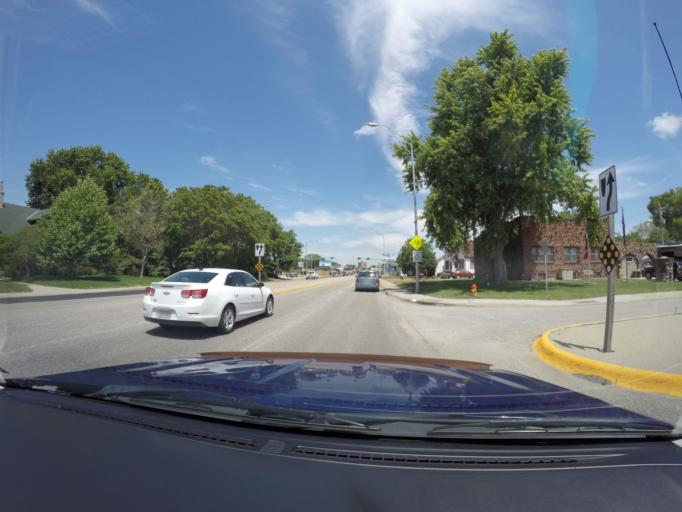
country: US
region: Nebraska
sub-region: Hall County
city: Grand Island
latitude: 40.9147
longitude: -98.3397
